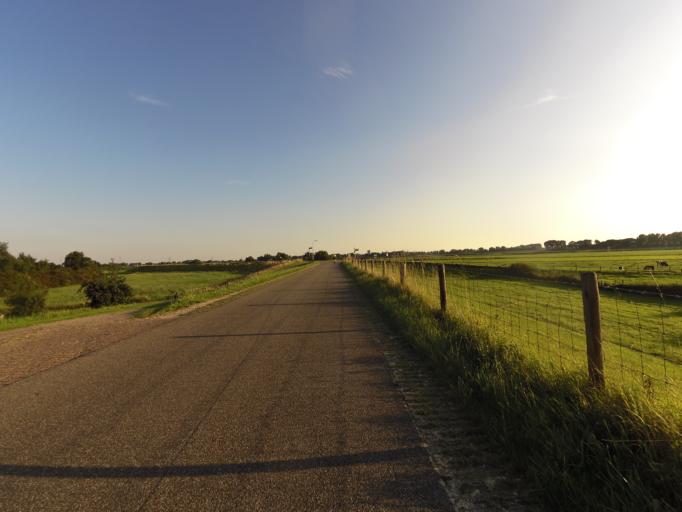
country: NL
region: Gelderland
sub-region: Gemeente Westervoort
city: Westervoort
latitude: 51.9365
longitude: 5.9689
